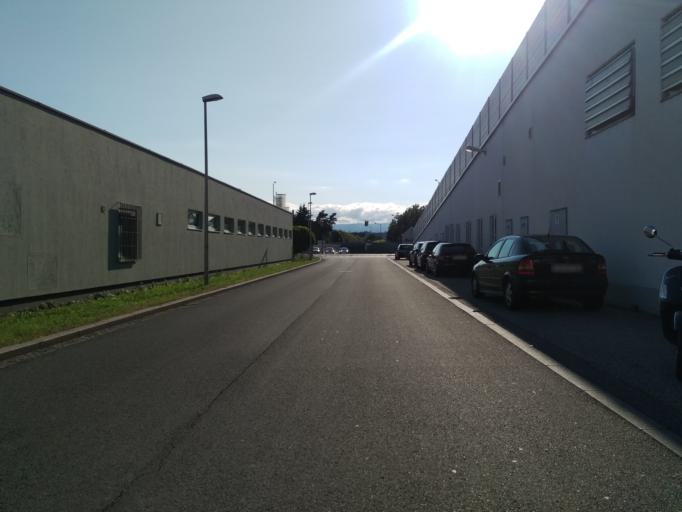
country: AT
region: Styria
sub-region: Politischer Bezirk Graz-Umgebung
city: Feldkirchen bei Graz
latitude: 47.0251
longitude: 15.4367
